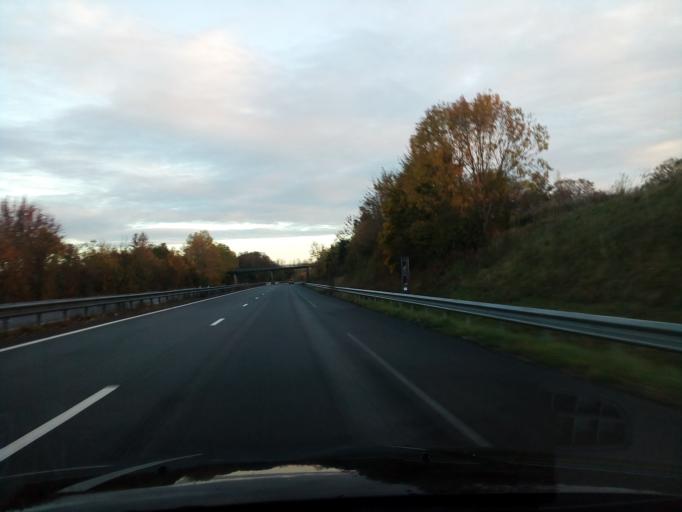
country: FR
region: Poitou-Charentes
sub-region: Departement de la Charente-Maritime
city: Chevanceaux
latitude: 45.3003
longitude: -0.2390
